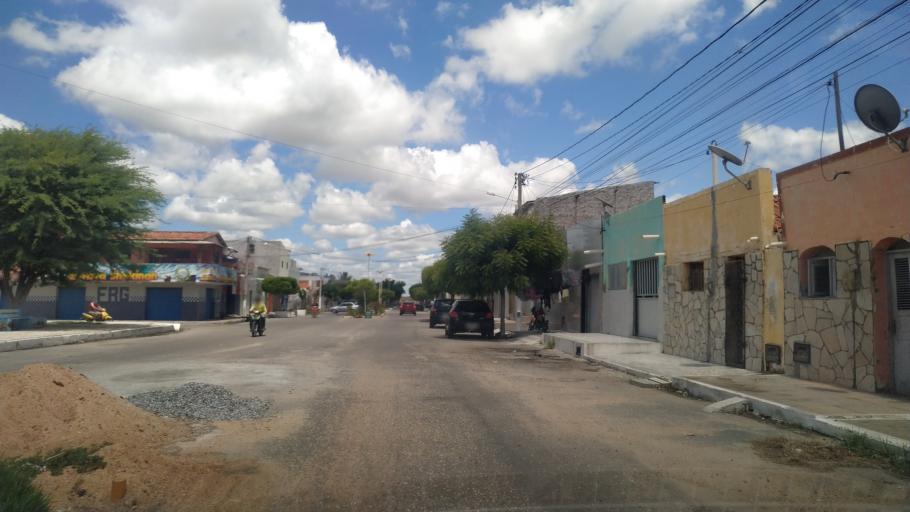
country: BR
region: Rio Grande do Norte
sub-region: Areia Branca
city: Areia Branca
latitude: -4.9557
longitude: -37.1310
